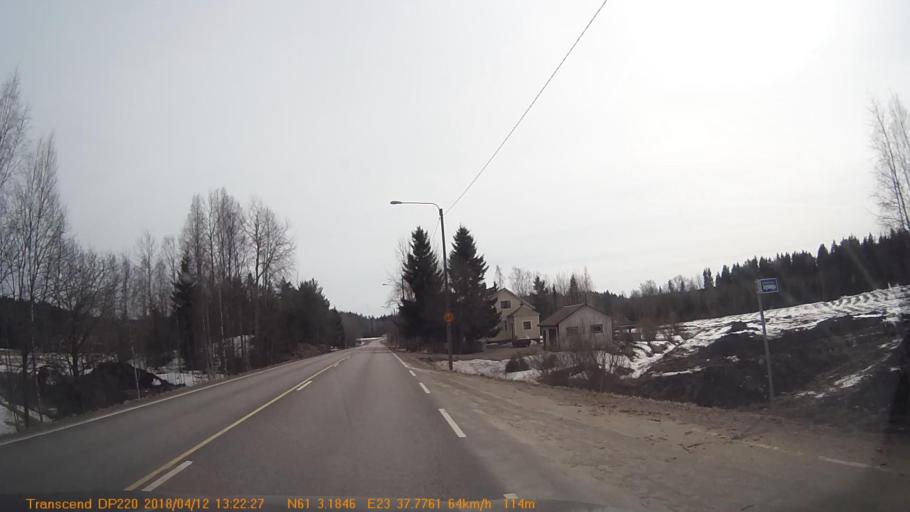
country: FI
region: Pirkanmaa
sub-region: Etelae-Pirkanmaa
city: Urjala
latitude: 61.0523
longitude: 23.6305
